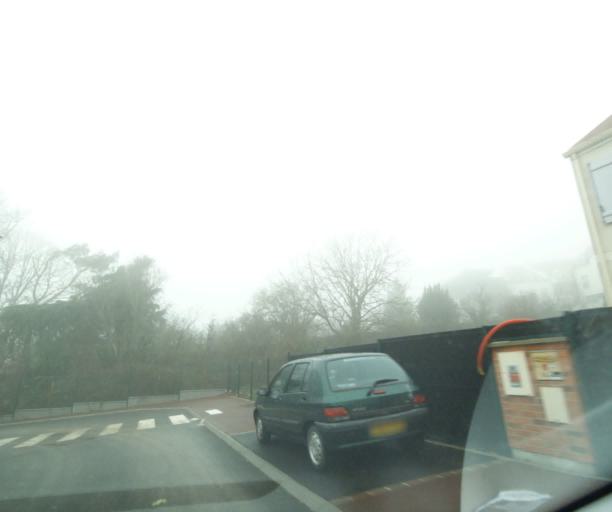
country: FR
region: Ile-de-France
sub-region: Departement de Seine-et-Marne
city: Dammartin-en-Goele
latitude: 49.0524
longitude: 2.6829
